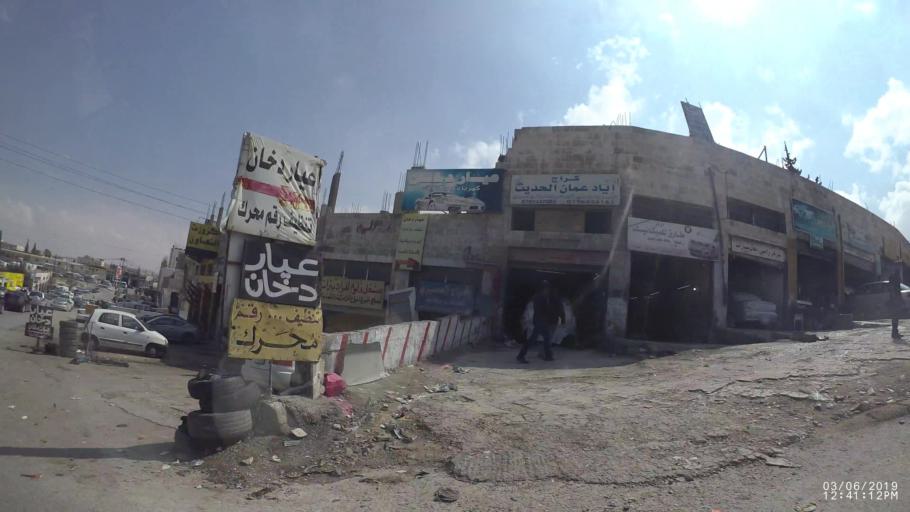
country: JO
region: Zarqa
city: Russeifa
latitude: 31.9906
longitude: 35.9998
